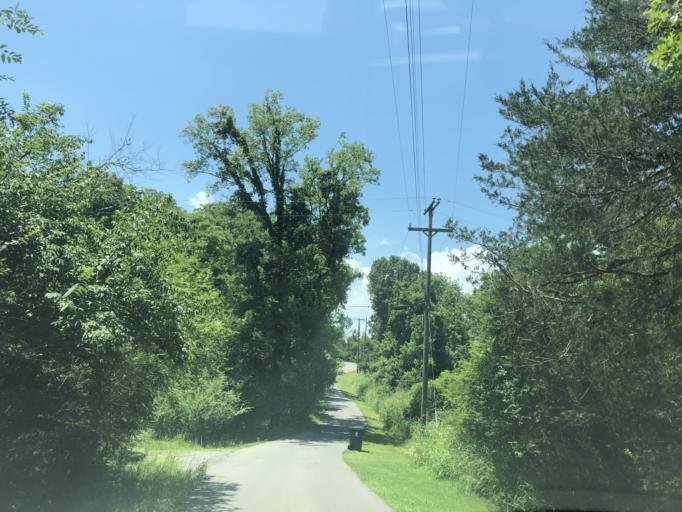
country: US
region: Tennessee
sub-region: Davidson County
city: Lakewood
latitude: 36.1717
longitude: -86.6340
